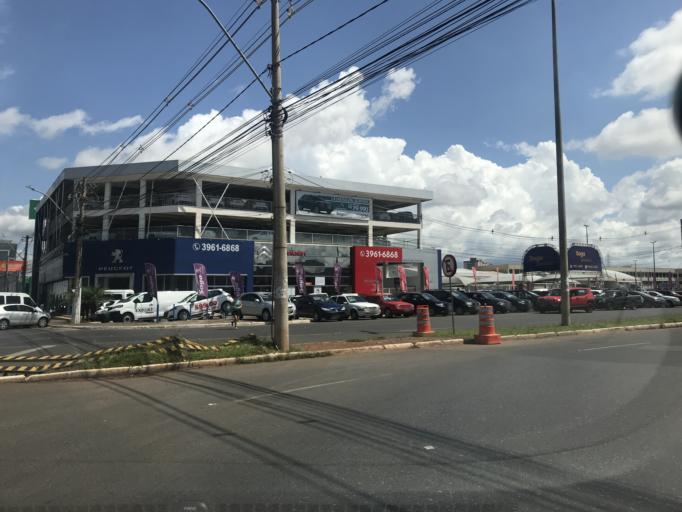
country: BR
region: Federal District
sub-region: Brasilia
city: Brasilia
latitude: -15.8494
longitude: -48.0417
